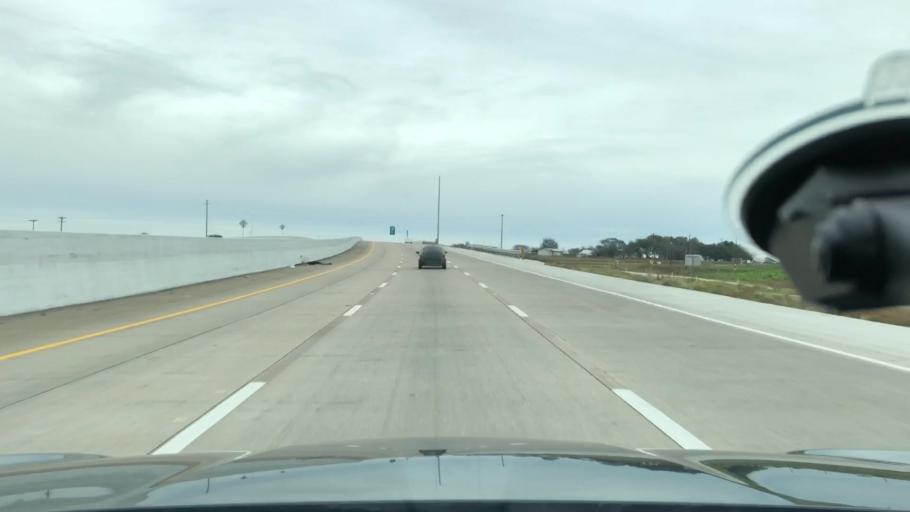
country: US
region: Texas
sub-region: Ellis County
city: Italy
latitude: 32.1743
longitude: -96.9104
